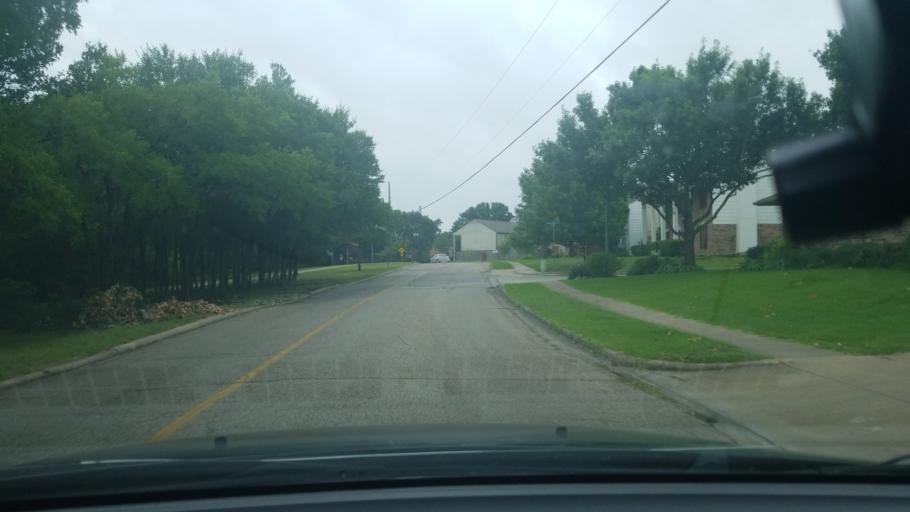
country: US
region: Texas
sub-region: Dallas County
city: Mesquite
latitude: 32.7901
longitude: -96.6473
